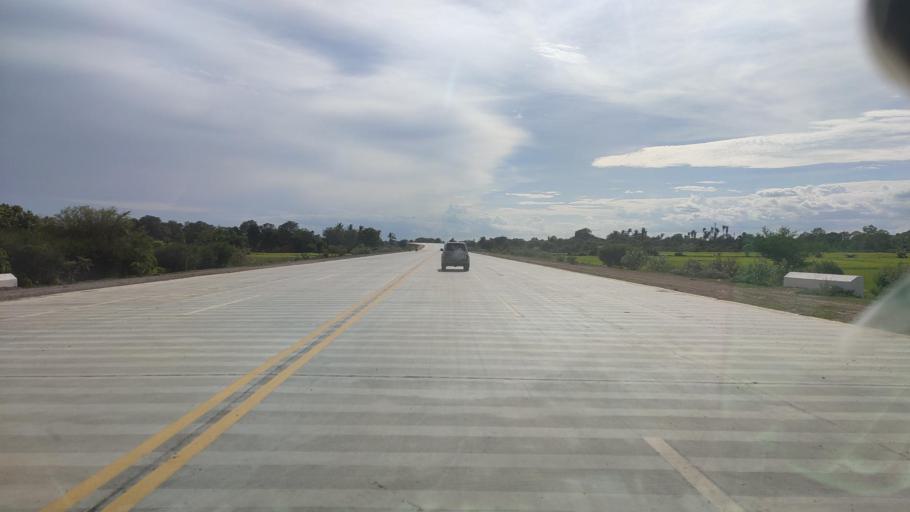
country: MM
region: Mandalay
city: Kyaukse
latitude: 21.5945
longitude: 96.1582
